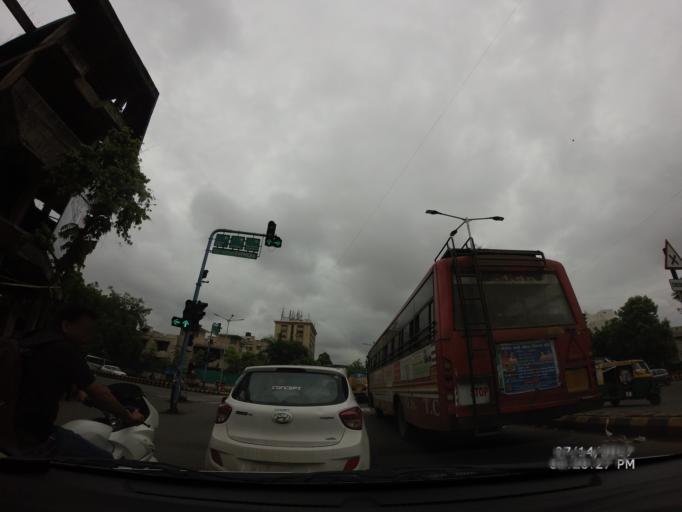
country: IN
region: Gujarat
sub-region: Ahmadabad
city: Ahmedabad
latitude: 23.0114
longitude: 72.5632
